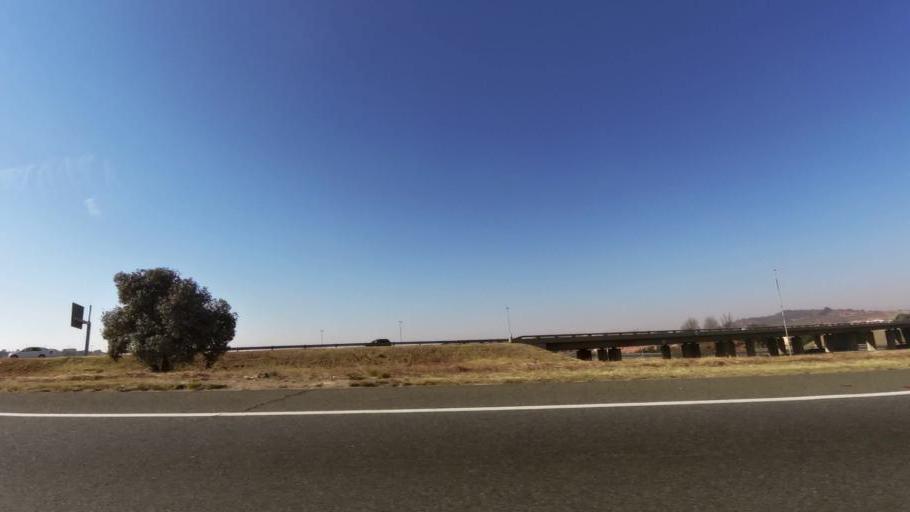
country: ZA
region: Gauteng
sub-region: City of Johannesburg Metropolitan Municipality
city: Johannesburg
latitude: -26.2619
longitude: 27.9849
